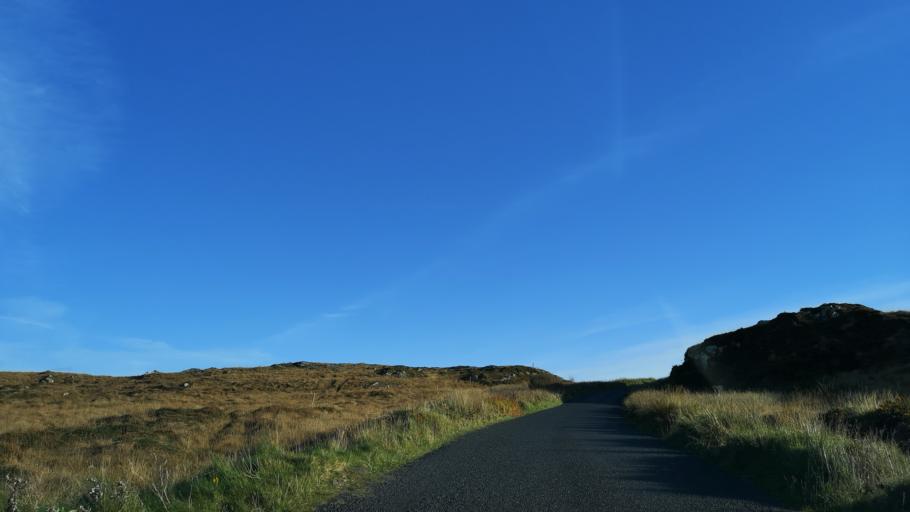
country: IE
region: Connaught
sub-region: County Galway
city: Clifden
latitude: 53.5041
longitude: -10.1032
